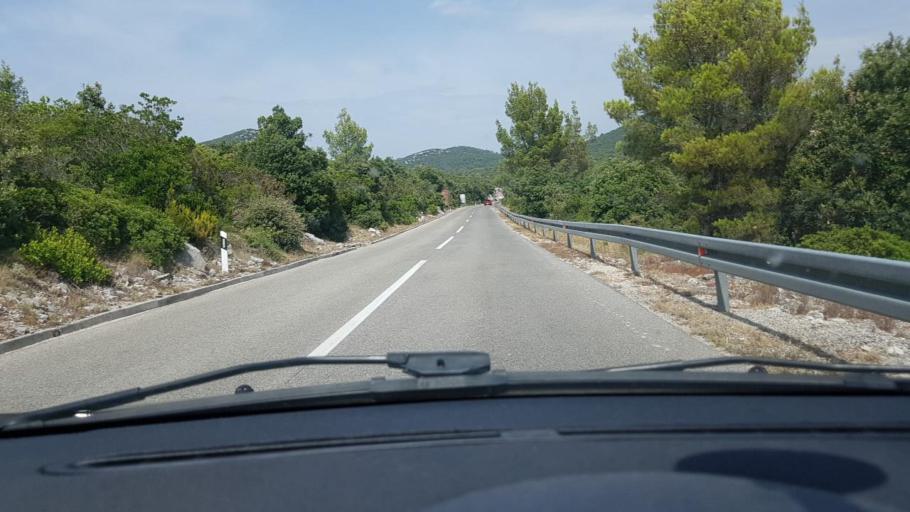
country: HR
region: Dubrovacko-Neretvanska
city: Smokvica
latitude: 42.9453
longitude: 16.9615
